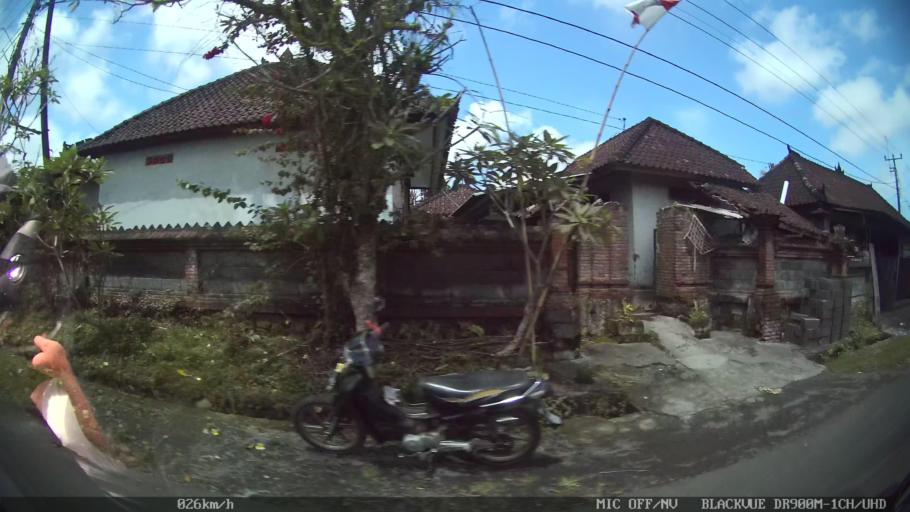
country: ID
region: Bali
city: Banjar Apuan Kaja
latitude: -8.5032
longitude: 115.3387
